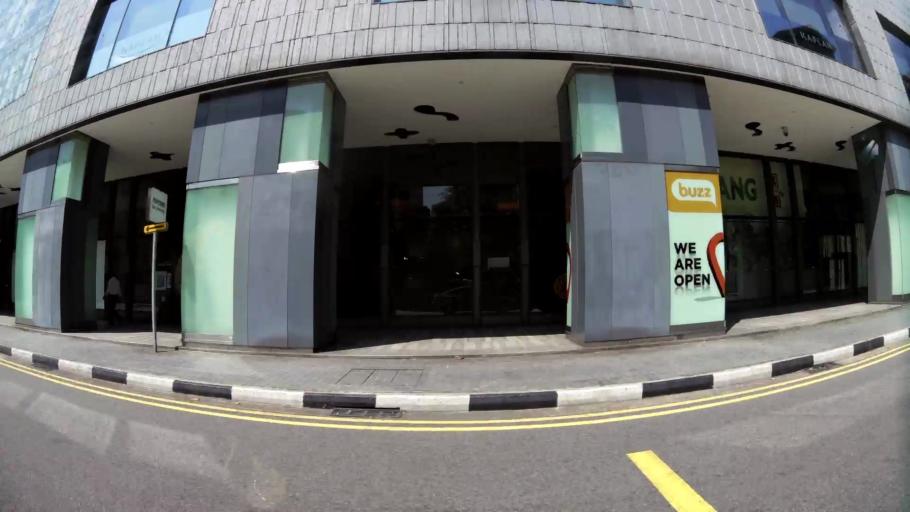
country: SG
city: Singapore
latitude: 1.3023
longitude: 103.8499
